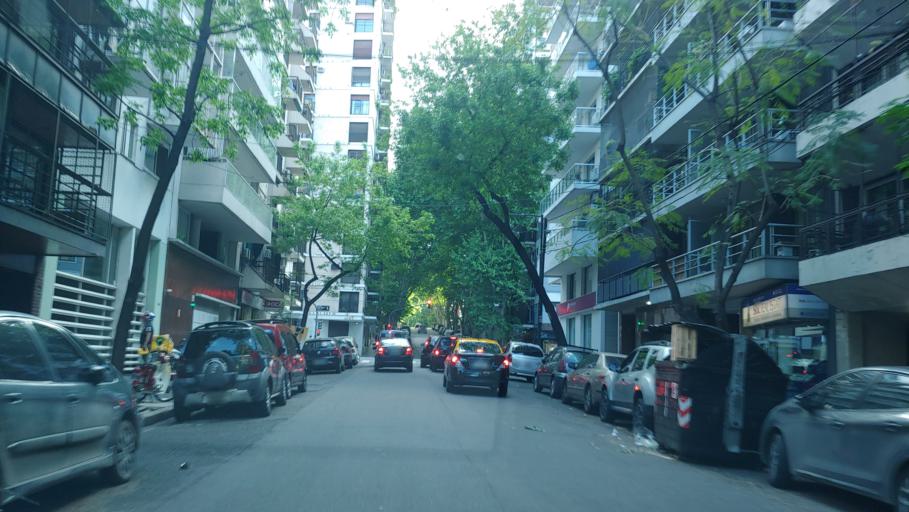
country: AR
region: Buenos Aires F.D.
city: Colegiales
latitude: -34.5642
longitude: -58.4408
